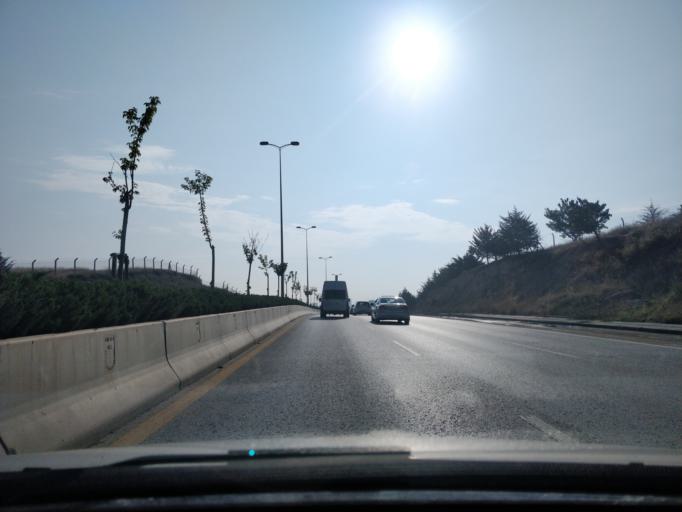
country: TR
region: Ankara
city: Etimesgut
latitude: 39.8963
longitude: 32.6649
